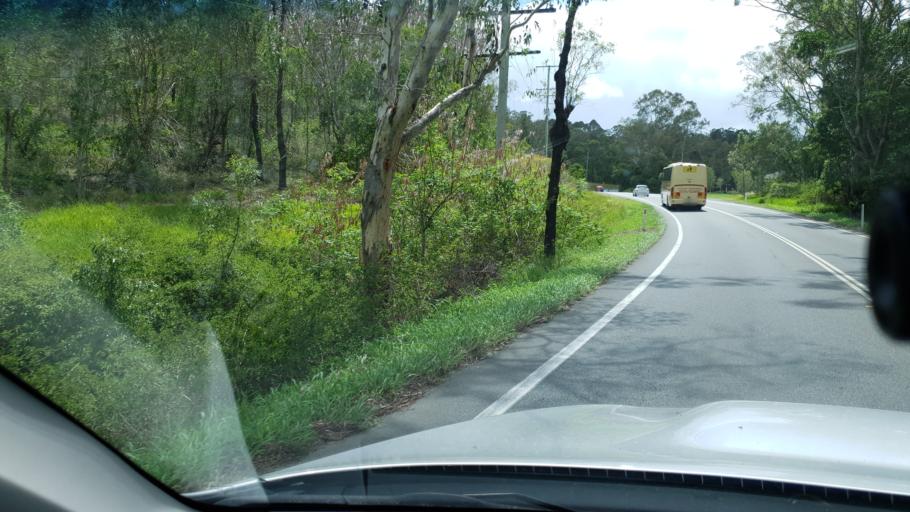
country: AU
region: Queensland
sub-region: Logan
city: Beenleigh
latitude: -27.6751
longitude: 153.2217
